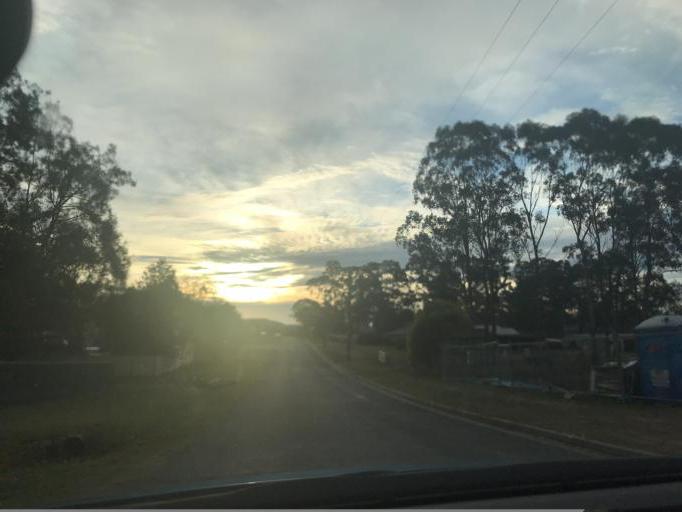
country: AU
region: New South Wales
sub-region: Cessnock
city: Cessnock
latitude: -32.9019
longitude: 151.2874
